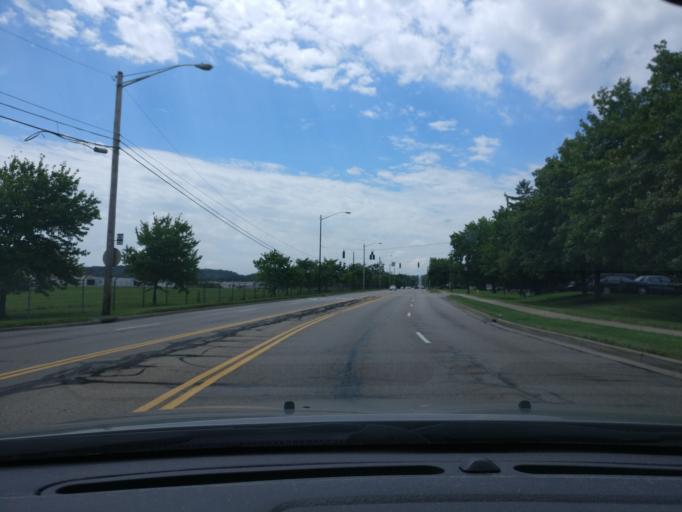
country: US
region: Ohio
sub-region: Montgomery County
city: West Carrollton City
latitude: 39.6732
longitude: -84.2408
